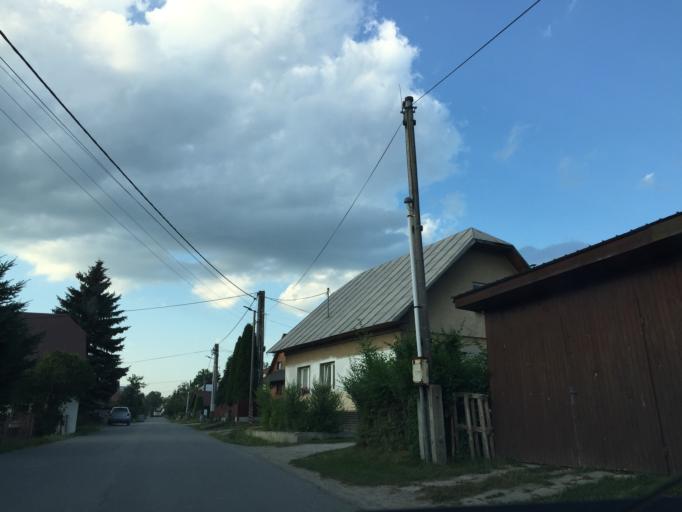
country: PL
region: Silesian Voivodeship
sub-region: Powiat zywiecki
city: Korbielow
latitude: 49.4729
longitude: 19.3821
